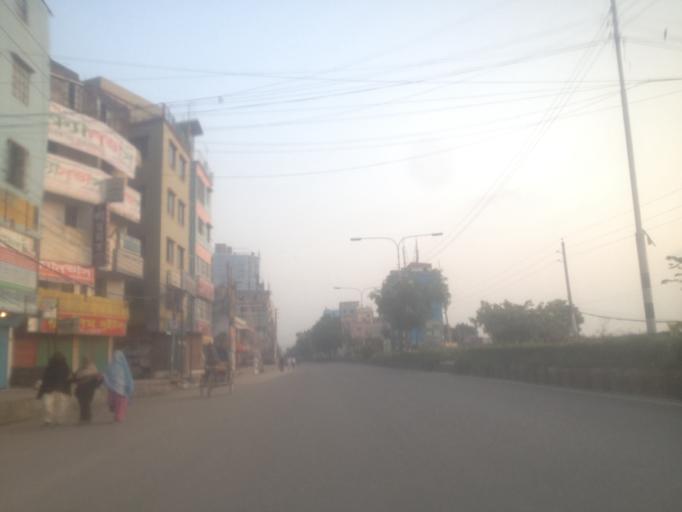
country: BD
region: Dhaka
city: Azimpur
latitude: 23.7841
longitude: 90.3783
